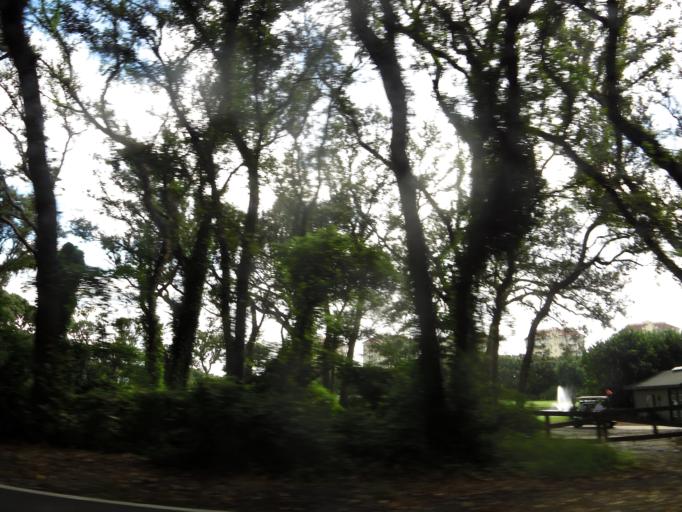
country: US
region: Florida
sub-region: Nassau County
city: Fernandina Beach
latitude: 30.5974
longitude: -81.4473
